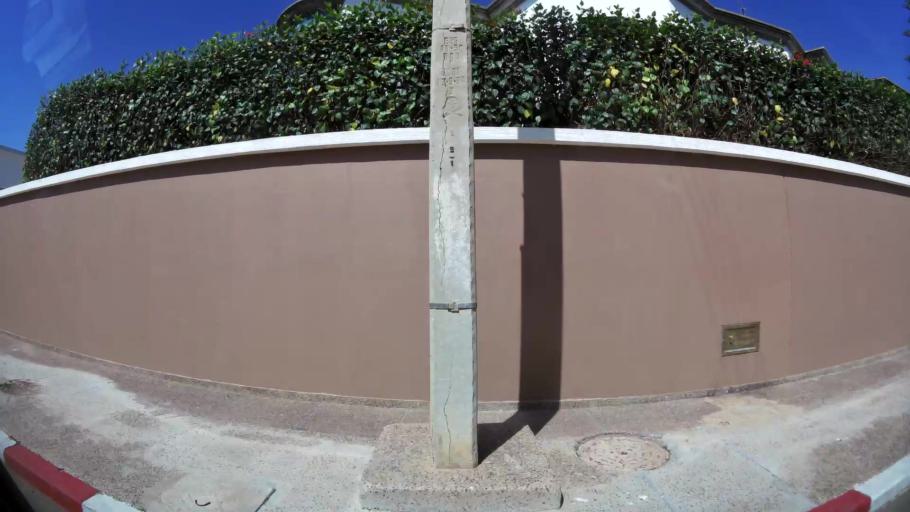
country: MA
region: Souss-Massa-Draa
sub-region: Inezgane-Ait Mellou
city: Inezgane
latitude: 30.3754
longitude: -9.5578
